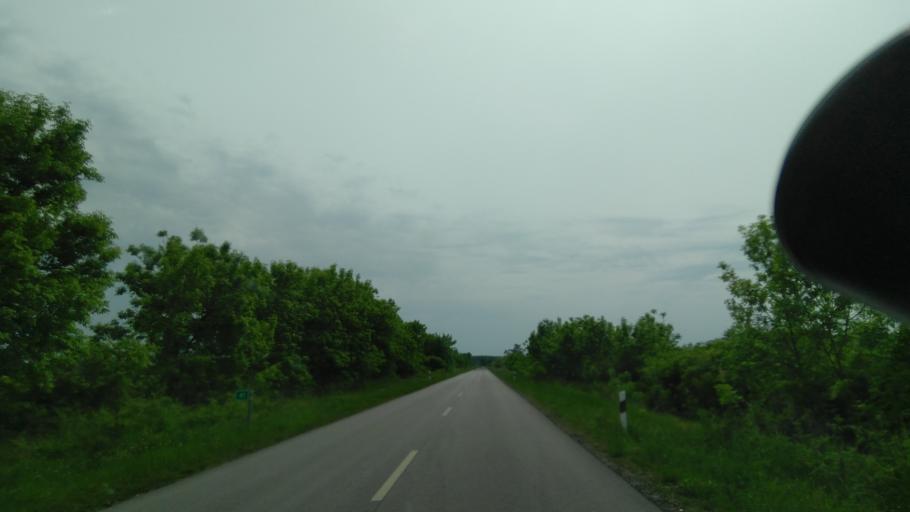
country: HU
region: Bekes
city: Mehkerek
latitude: 46.8340
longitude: 21.4261
